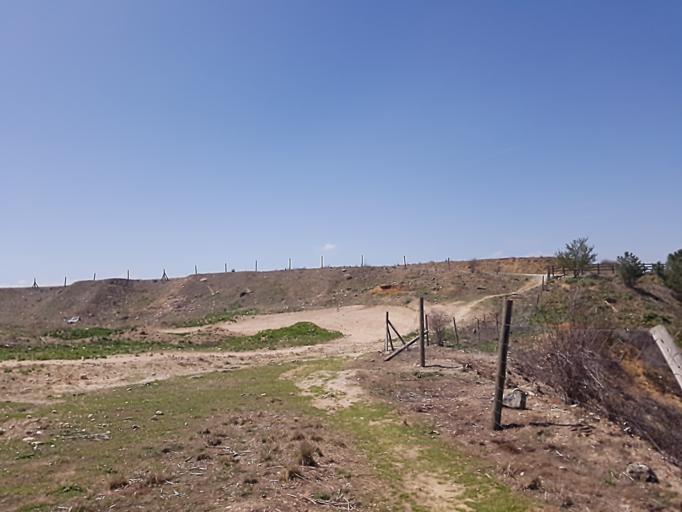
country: ES
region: Castille and Leon
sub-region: Provincia de Segovia
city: Segovia
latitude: 40.9464
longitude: -4.1302
